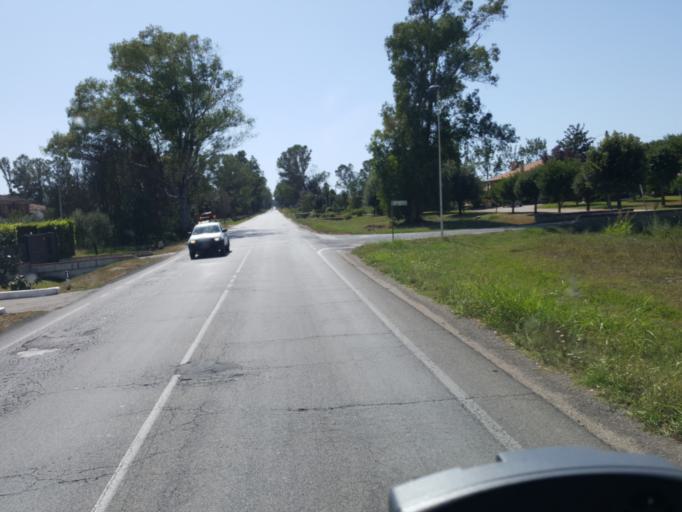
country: IT
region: Latium
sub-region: Provincia di Latina
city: Pontinia
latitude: 41.3517
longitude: 13.0980
